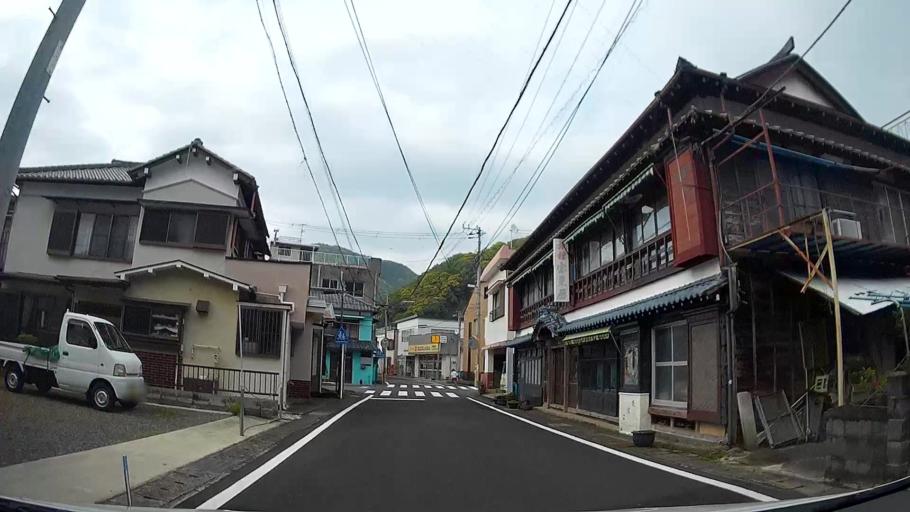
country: JP
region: Shizuoka
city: Heda
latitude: 34.8252
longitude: 138.7678
